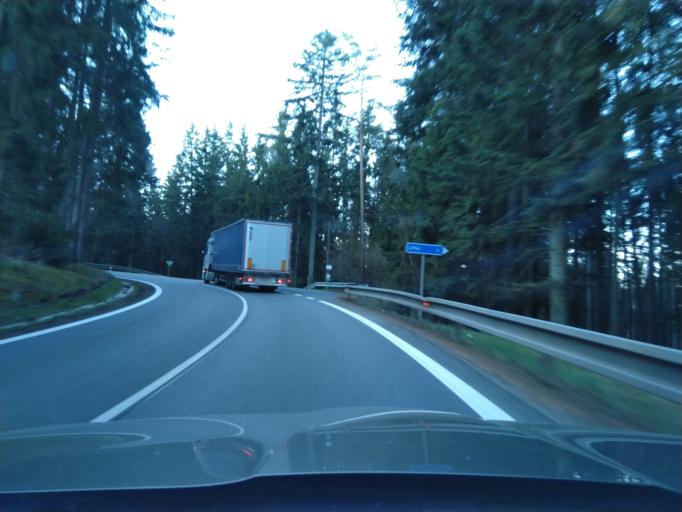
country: CZ
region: Jihocesky
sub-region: Okres Prachatice
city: Vimperk
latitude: 49.0404
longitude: 13.7605
